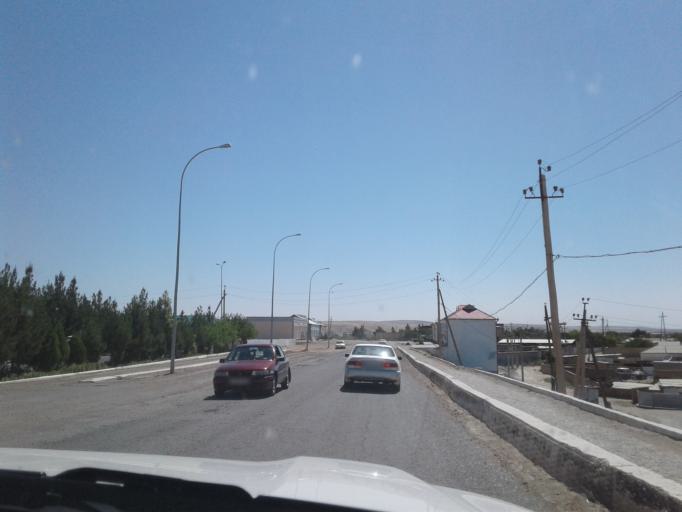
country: AF
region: Badghis
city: Bala Murghab
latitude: 35.9549
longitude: 62.9084
